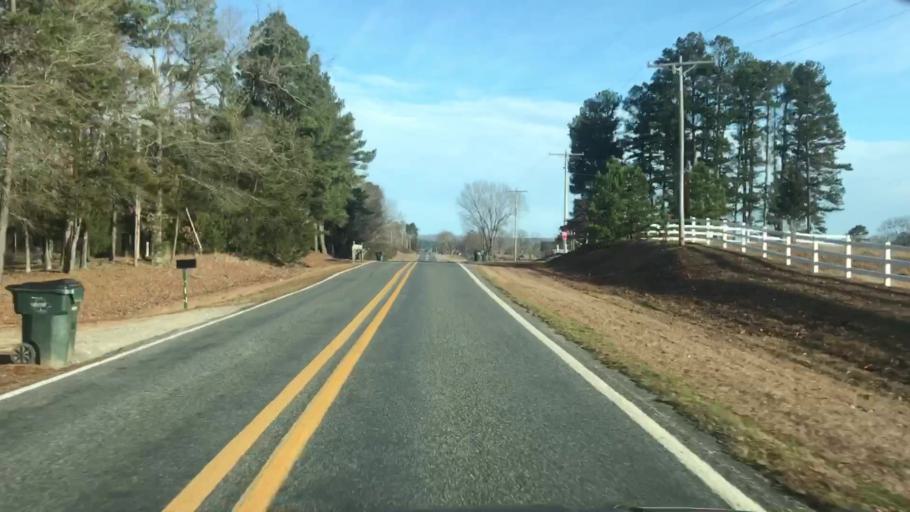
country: US
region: Arkansas
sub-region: Garland County
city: Rockwell
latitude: 34.4972
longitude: -93.2765
